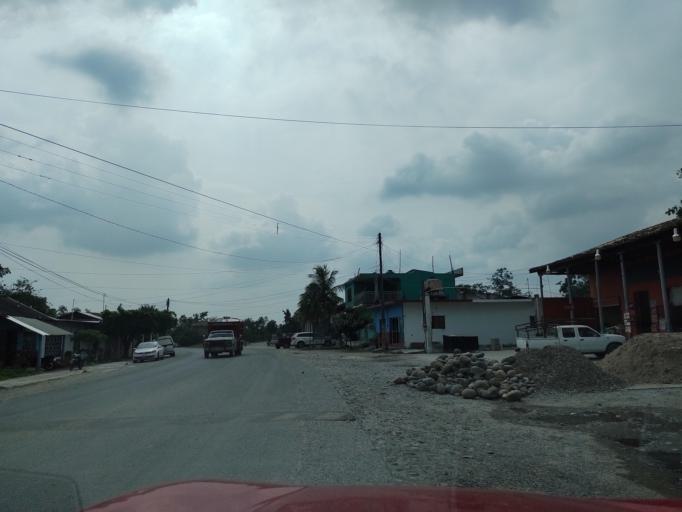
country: MX
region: Veracruz
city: Agua Dulce
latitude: 20.3629
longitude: -97.2952
